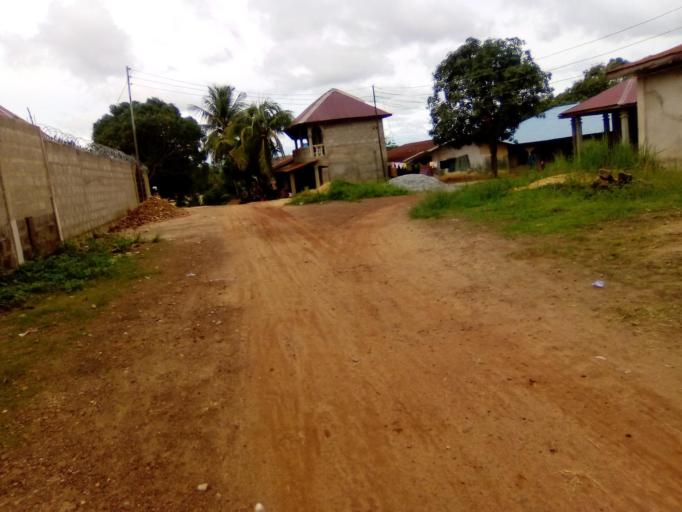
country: SL
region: Southern Province
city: Bo
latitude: 7.9453
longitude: -11.7186
